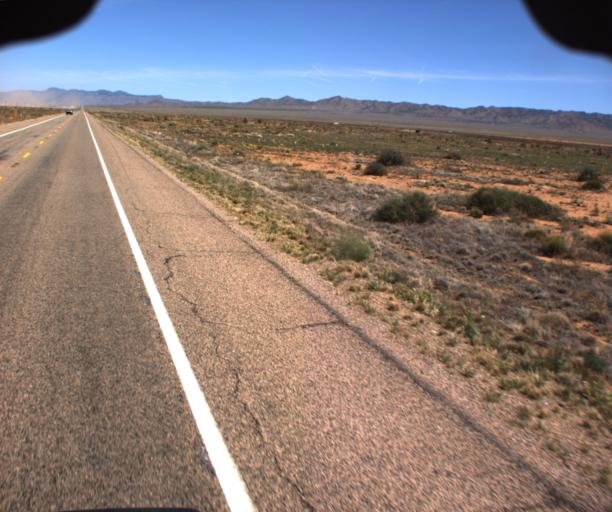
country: US
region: Arizona
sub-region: Mohave County
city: New Kingman-Butler
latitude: 35.3123
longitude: -113.9198
